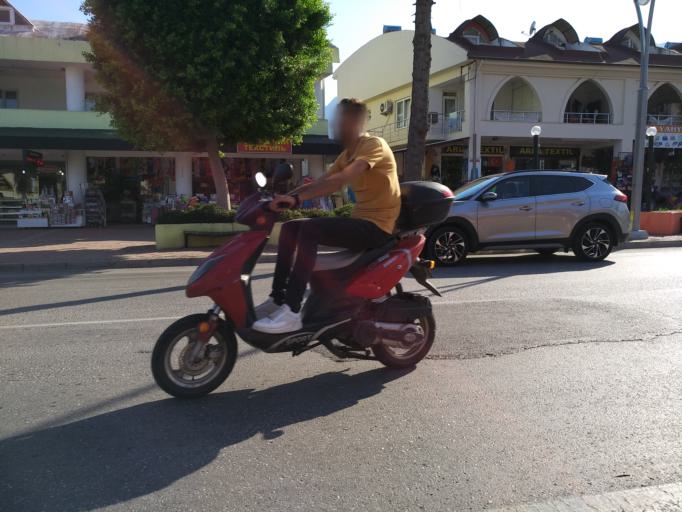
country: TR
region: Antalya
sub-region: Kemer
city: Goeynuek
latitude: 36.6652
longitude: 30.5547
